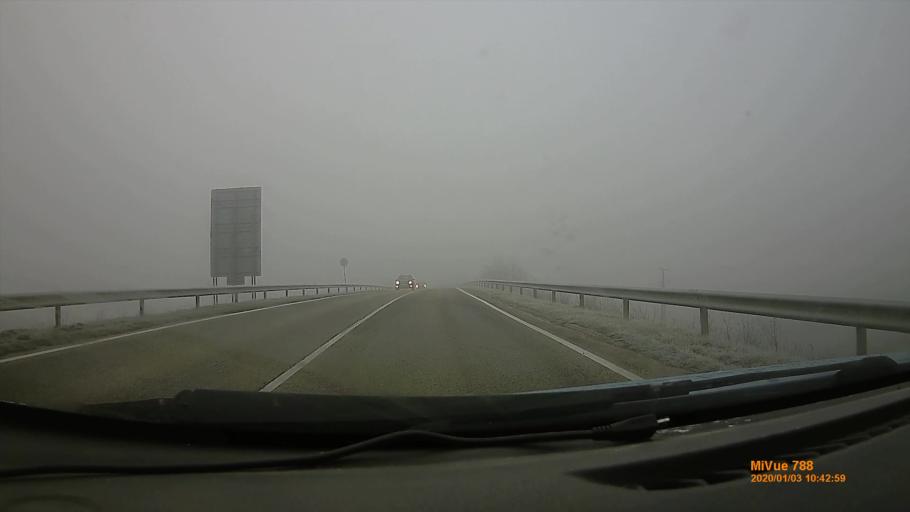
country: HU
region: Tolna
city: Bataszek
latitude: 46.2074
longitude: 18.7071
